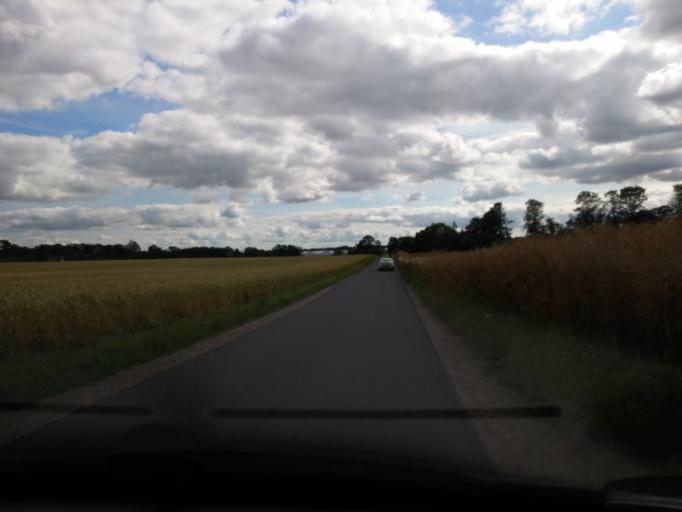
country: DK
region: South Denmark
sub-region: Kerteminde Kommune
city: Munkebo
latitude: 55.4084
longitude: 10.5631
